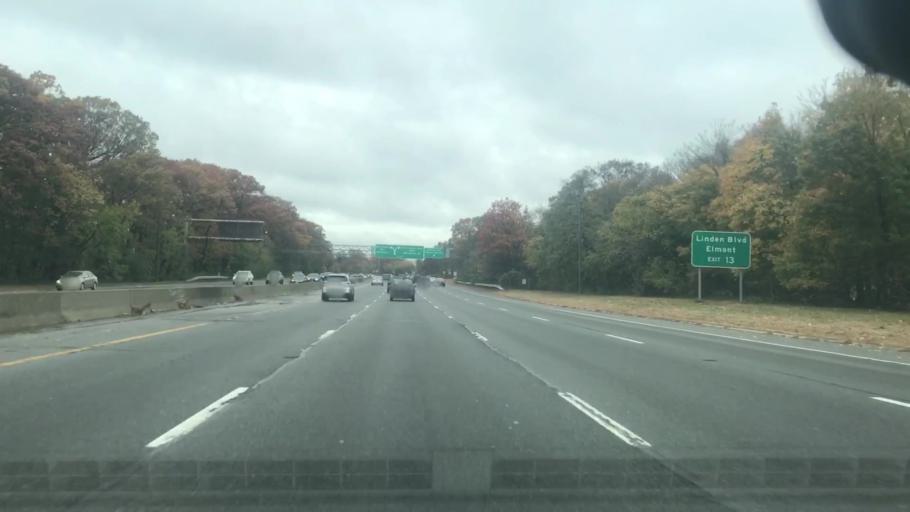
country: US
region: New York
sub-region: Nassau County
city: North Valley Stream
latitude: 40.6846
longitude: -73.7093
